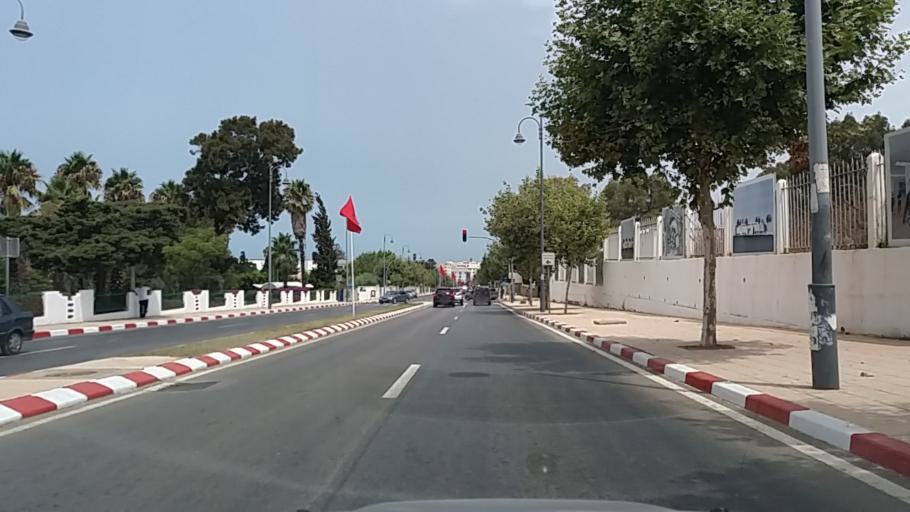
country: MA
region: Tanger-Tetouan
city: Asilah
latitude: 35.4647
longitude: -6.0305
